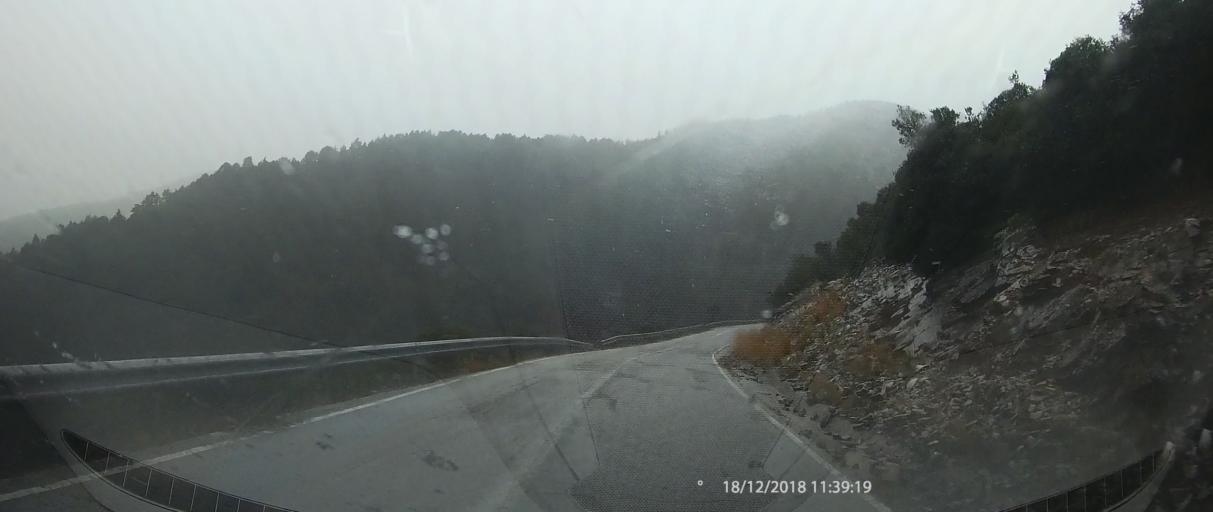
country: GR
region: Central Macedonia
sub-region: Nomos Pierias
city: Litochoro
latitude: 40.1090
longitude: 22.4797
